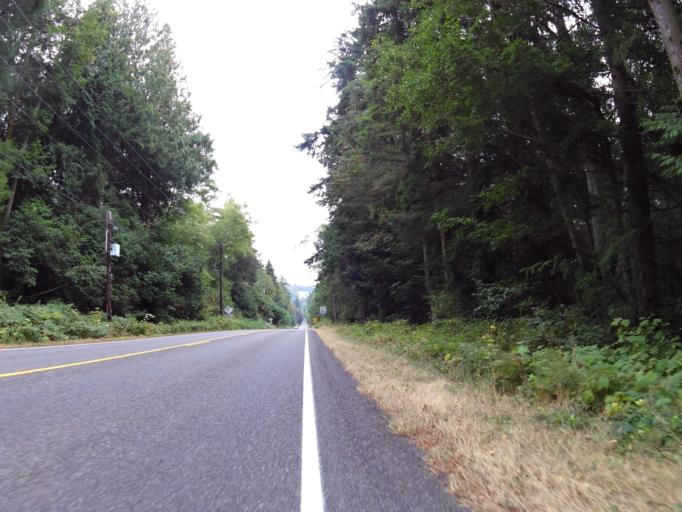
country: US
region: Washington
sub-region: Jefferson County
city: Port Ludlow
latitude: 47.9651
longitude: -122.6977
